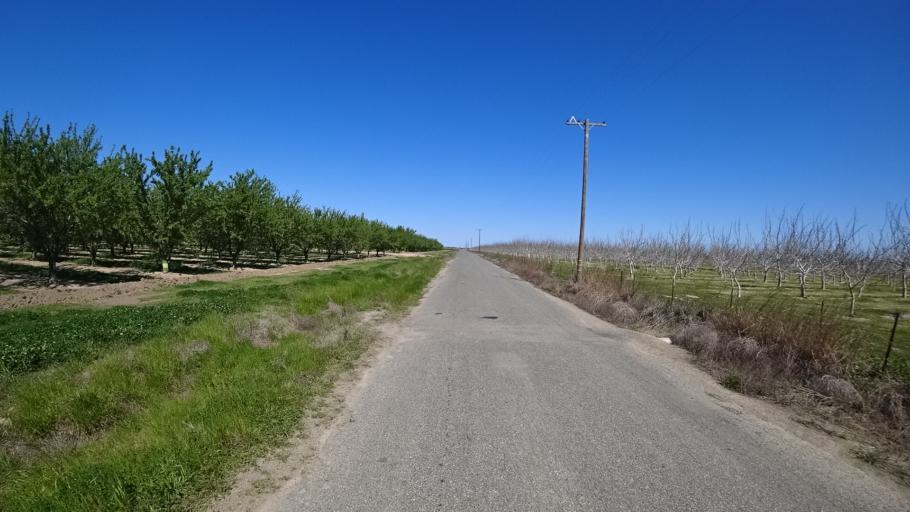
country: US
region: California
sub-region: Glenn County
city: Orland
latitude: 39.6837
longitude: -122.2342
